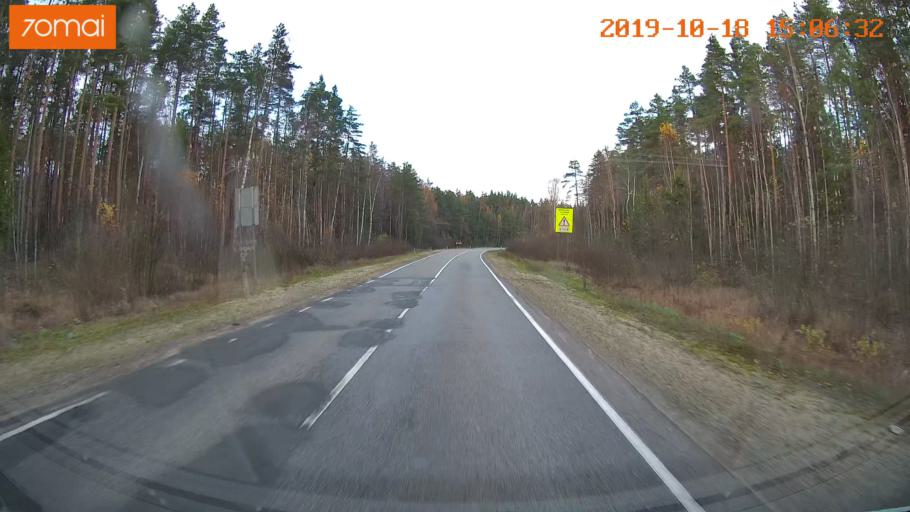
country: RU
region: Vladimir
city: Gus'-Khrustal'nyy
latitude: 55.5315
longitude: 40.5793
